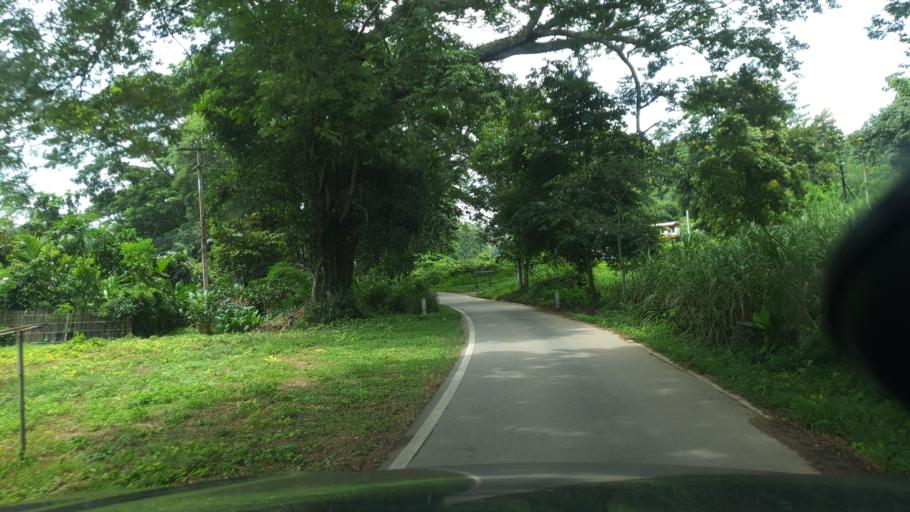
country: TH
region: Lampang
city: Hang Chat
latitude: 18.4033
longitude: 99.2623
